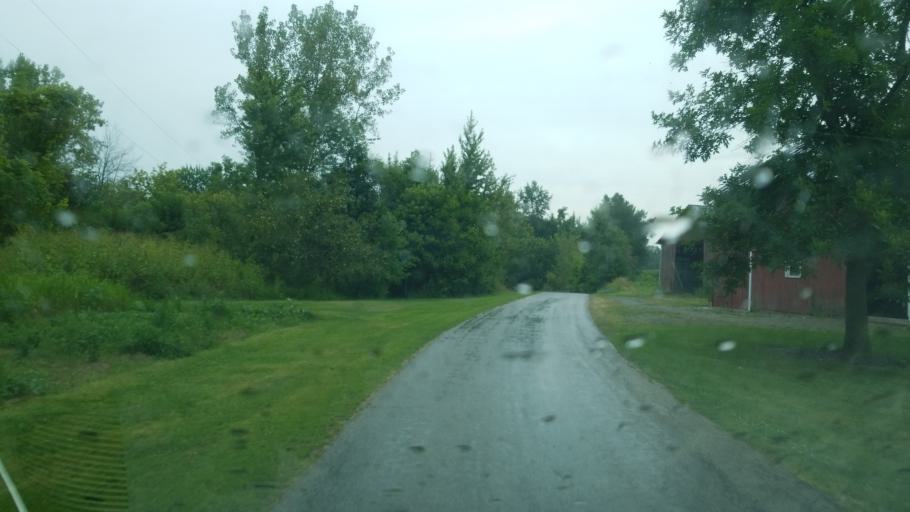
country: US
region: Ohio
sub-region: Huron County
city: Willard
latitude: 40.9330
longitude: -82.7859
